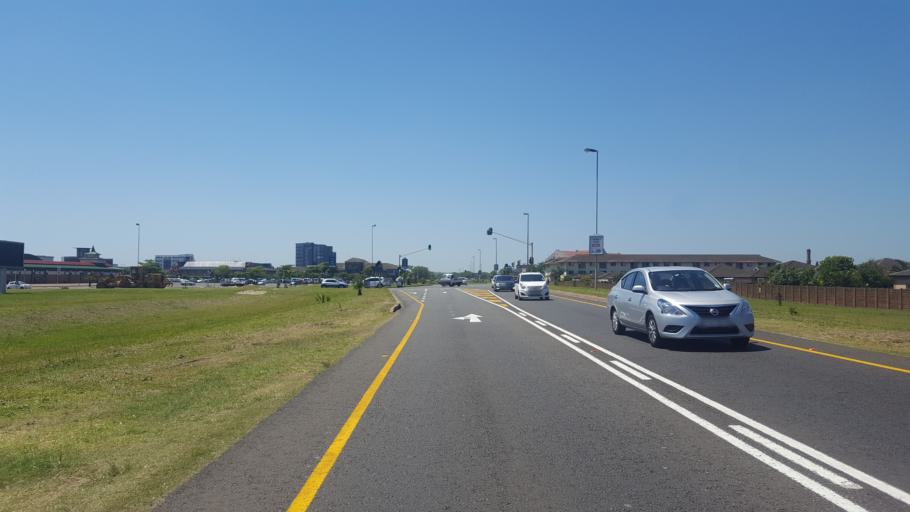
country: ZA
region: KwaZulu-Natal
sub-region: uThungulu District Municipality
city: Richards Bay
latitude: -28.7565
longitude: 32.0527
